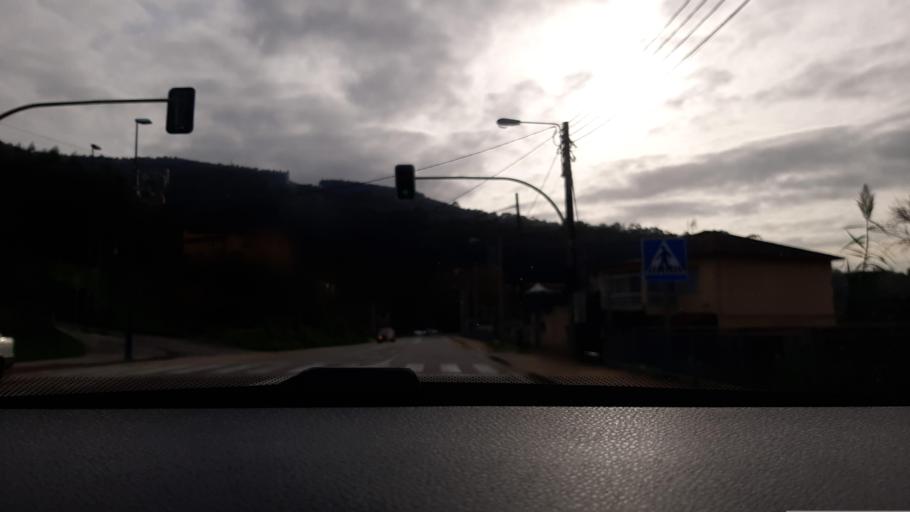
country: ES
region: Galicia
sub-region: Provincia de Pontevedra
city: Nigran
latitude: 42.1852
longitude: -8.7876
